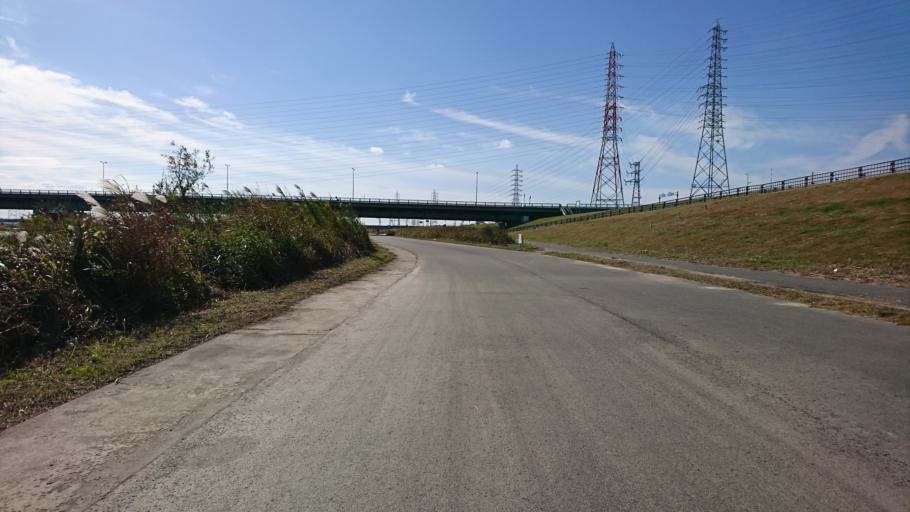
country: JP
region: Hyogo
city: Kakogawacho-honmachi
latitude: 34.7679
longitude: 134.8092
